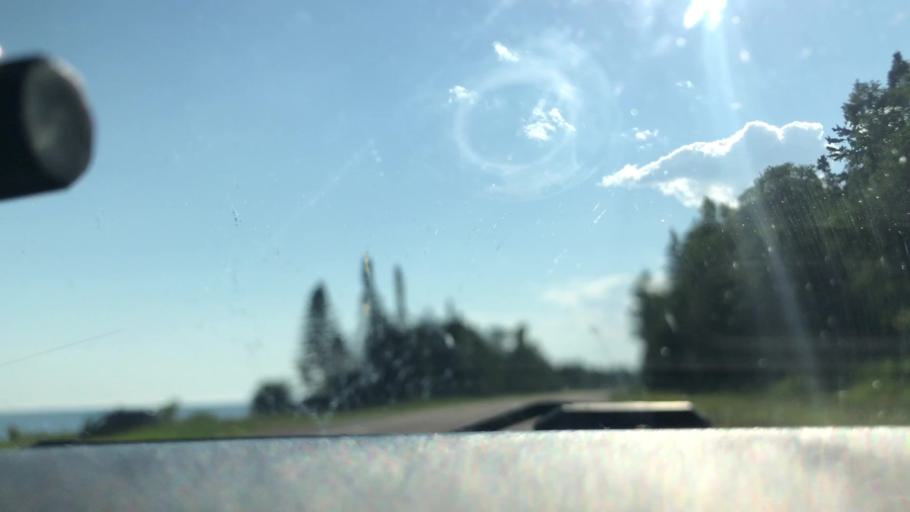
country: US
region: Minnesota
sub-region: Cook County
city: Grand Marais
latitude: 47.7978
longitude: -90.1095
